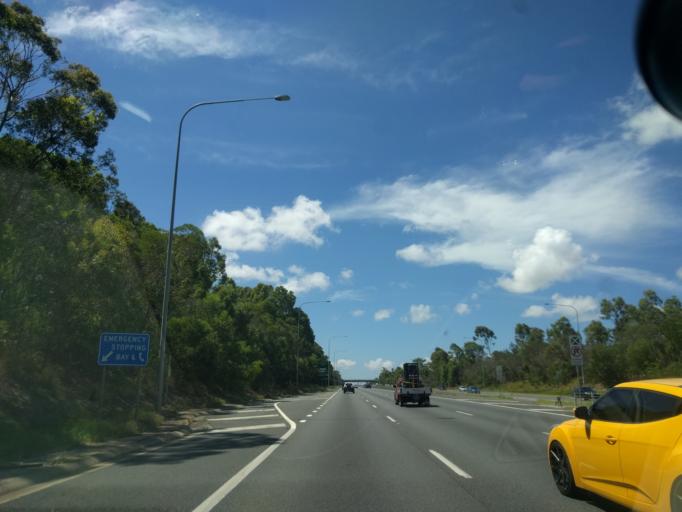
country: AU
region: Queensland
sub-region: Moreton Bay
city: Murrumba Downs
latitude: -27.2663
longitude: 153.0180
